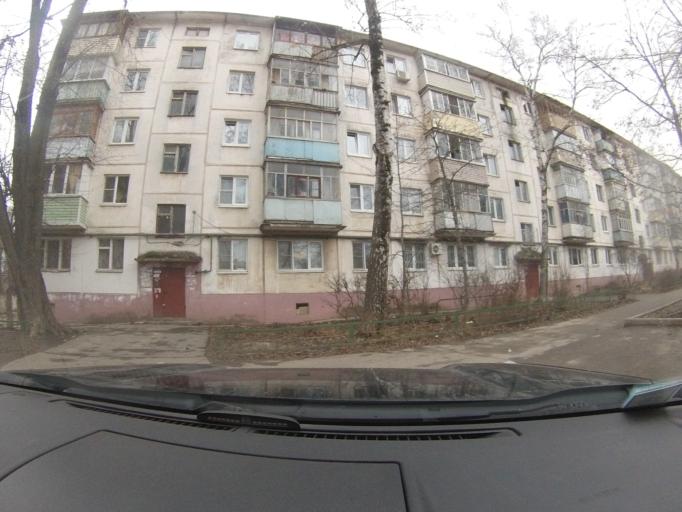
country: RU
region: Moskovskaya
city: Peski
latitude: 55.2727
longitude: 38.7445
